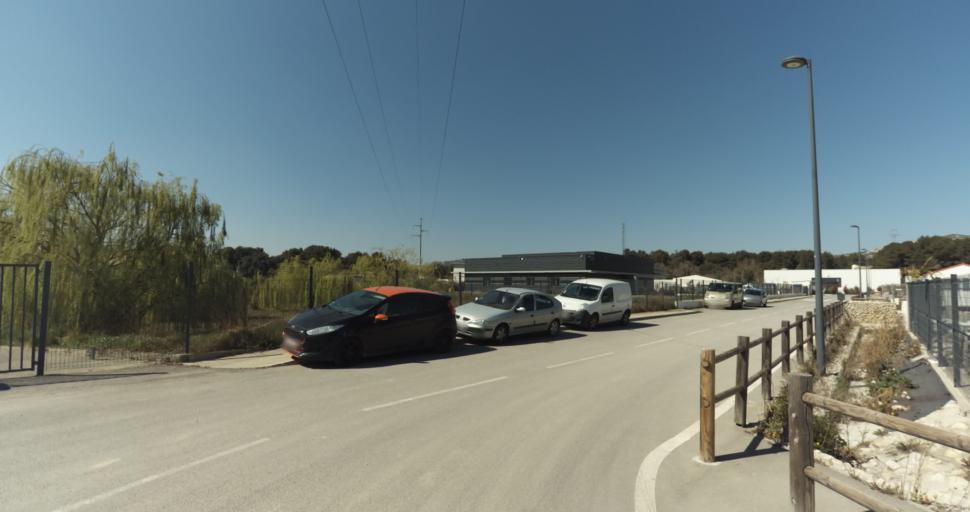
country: FR
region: Provence-Alpes-Cote d'Azur
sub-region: Departement des Bouches-du-Rhone
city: Pelissanne
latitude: 43.6350
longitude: 5.1724
